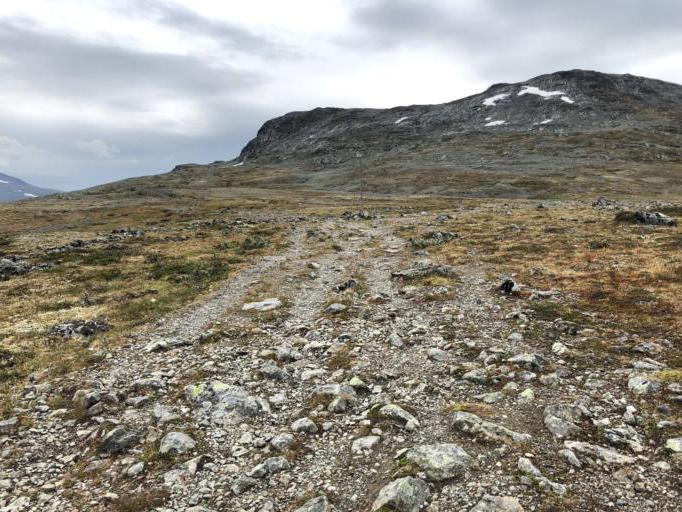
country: NO
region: Oppland
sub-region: Lom
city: Fossbergom
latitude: 61.5223
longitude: 8.8102
